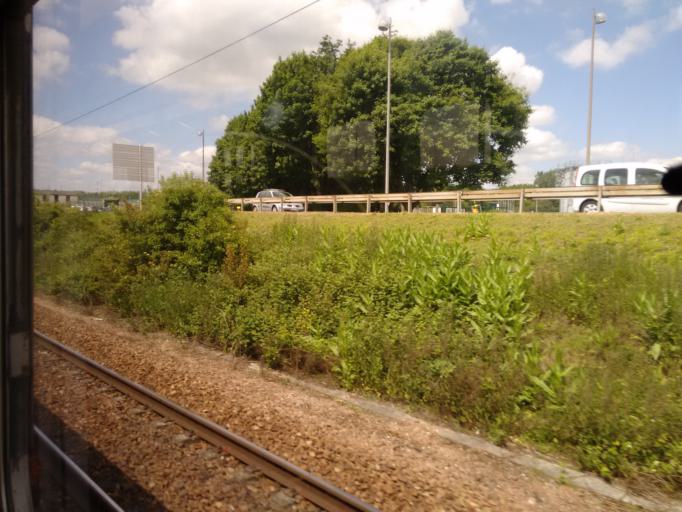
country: FR
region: Ile-de-France
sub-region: Departement du Val-d'Oise
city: Roissy-en-France
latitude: 49.0061
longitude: 2.5370
